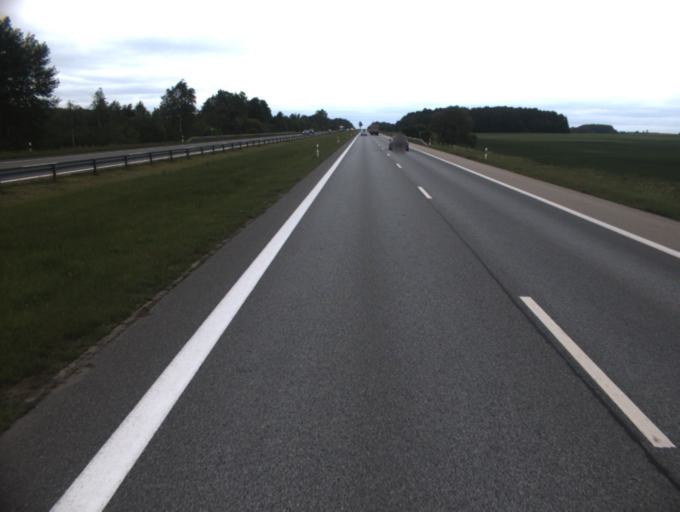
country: LT
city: Raseiniai
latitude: 55.3103
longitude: 23.2416
